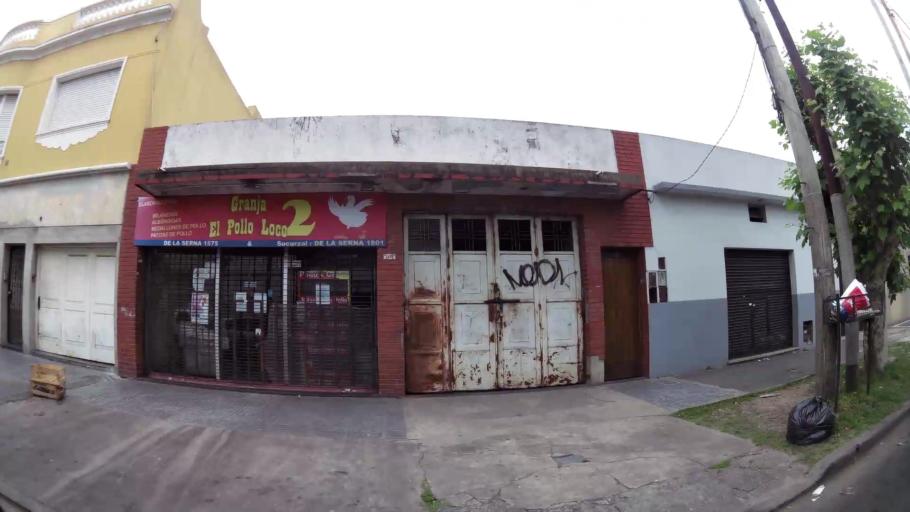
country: AR
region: Buenos Aires
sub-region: Partido de Avellaneda
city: Avellaneda
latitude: -34.6891
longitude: -58.3679
